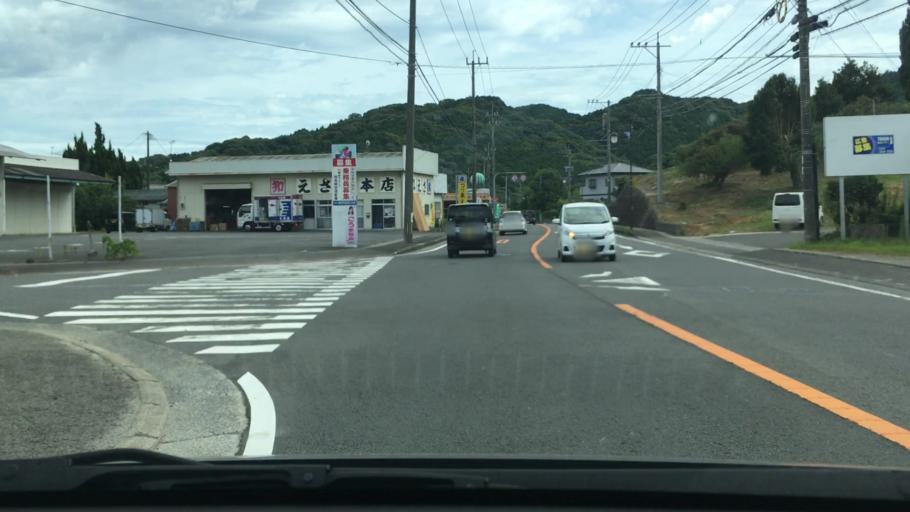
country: JP
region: Nagasaki
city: Togitsu
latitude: 32.8967
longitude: 129.7807
